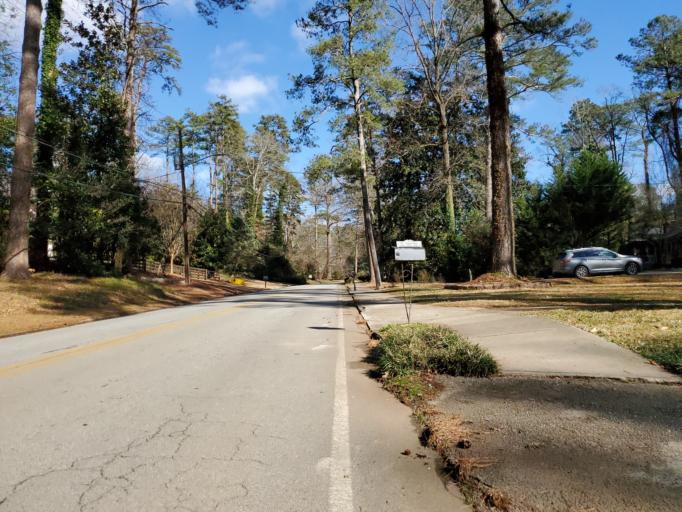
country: US
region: Georgia
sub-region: DeKalb County
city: Belvedere Park
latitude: 33.7581
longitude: -84.2851
